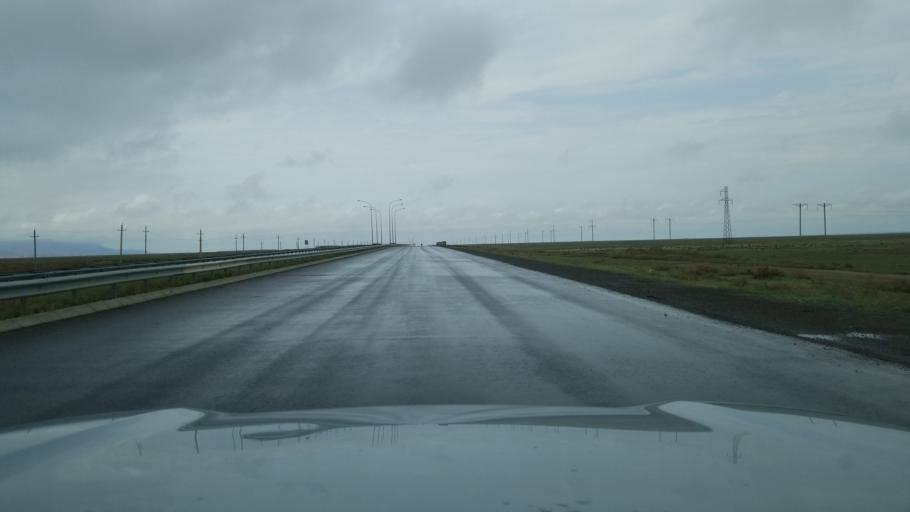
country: TM
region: Balkan
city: Gazanjyk
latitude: 39.1508
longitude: 55.8553
